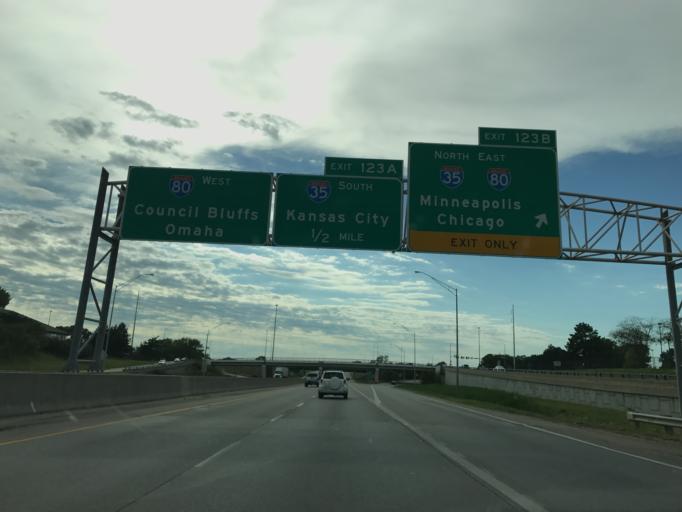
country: US
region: Iowa
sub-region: Polk County
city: Clive
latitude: 41.5924
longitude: -93.7676
